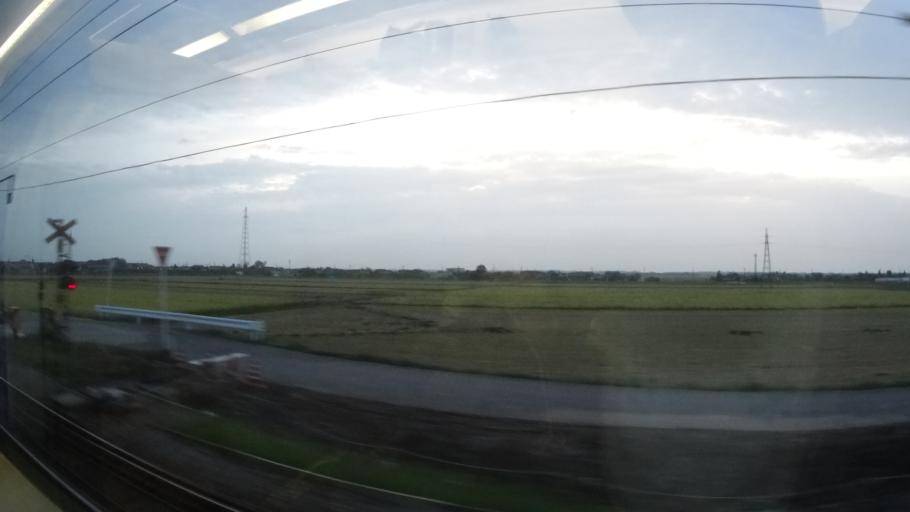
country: JP
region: Niigata
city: Shibata
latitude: 38.0233
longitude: 139.3810
